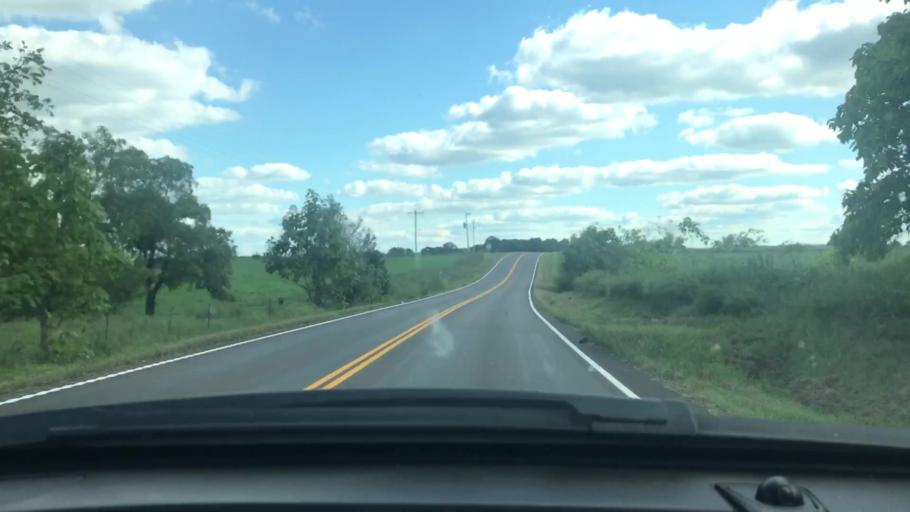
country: US
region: Missouri
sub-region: Wright County
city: Mountain Grove
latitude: 37.2936
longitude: -92.3085
